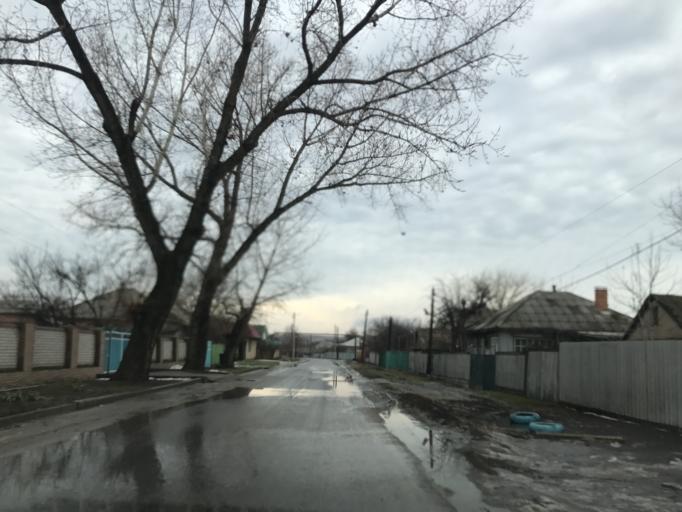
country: RU
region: Rostov
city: Glubokiy
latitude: 48.5247
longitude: 40.3146
